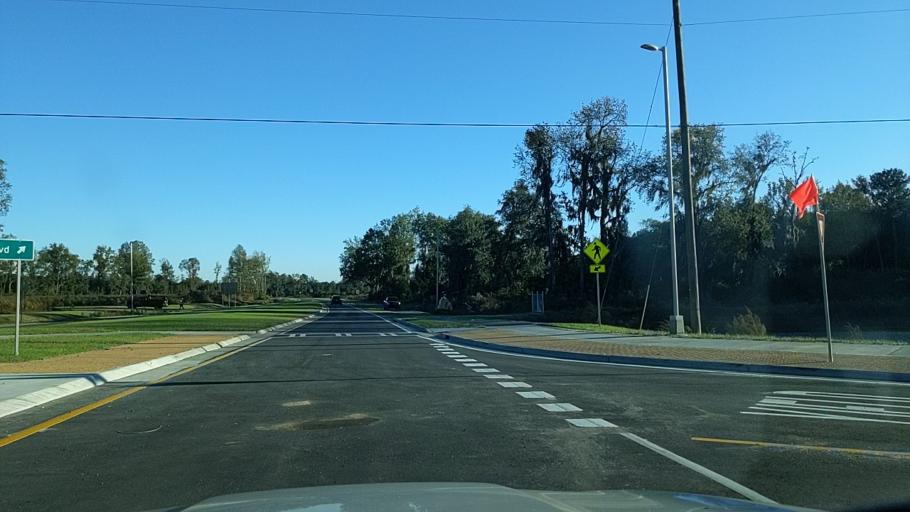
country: US
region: Georgia
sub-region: Chatham County
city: Port Wentworth
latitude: 32.1926
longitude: -81.2235
